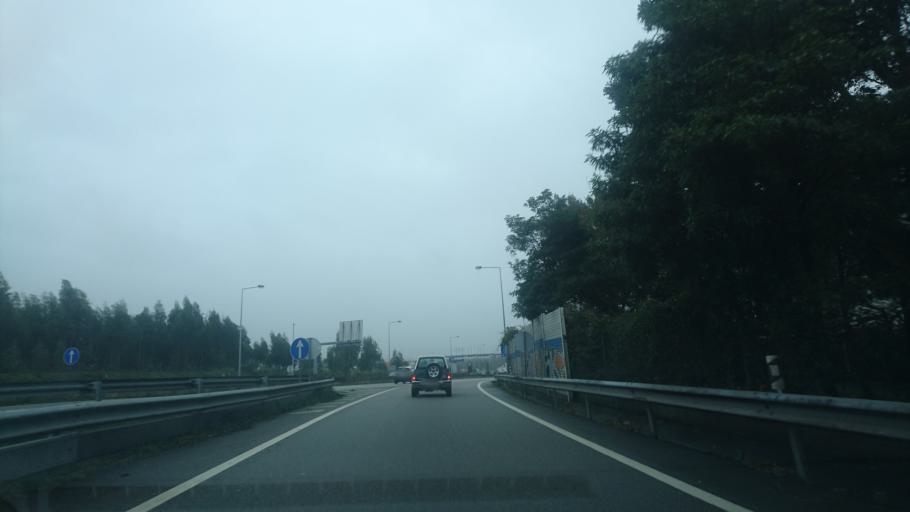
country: PT
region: Porto
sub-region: Vila Nova de Gaia
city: Vila Nova de Gaia
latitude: 41.1134
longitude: -8.6267
